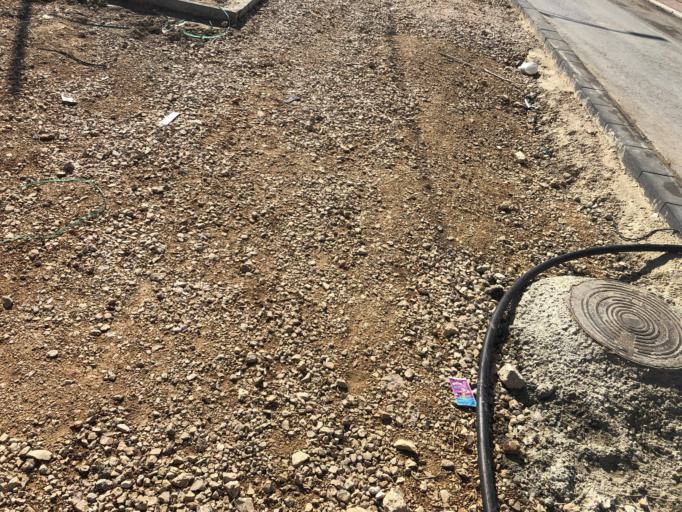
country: IL
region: Jerusalem
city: Modiin Ilit
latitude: 31.9261
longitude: 35.0465
